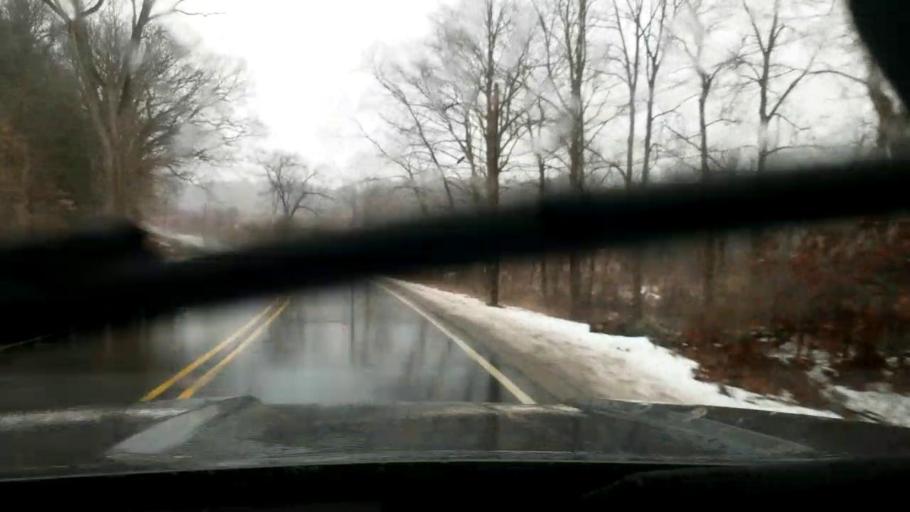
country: US
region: Michigan
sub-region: Jackson County
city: Grass Lake
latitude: 42.3249
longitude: -84.2093
